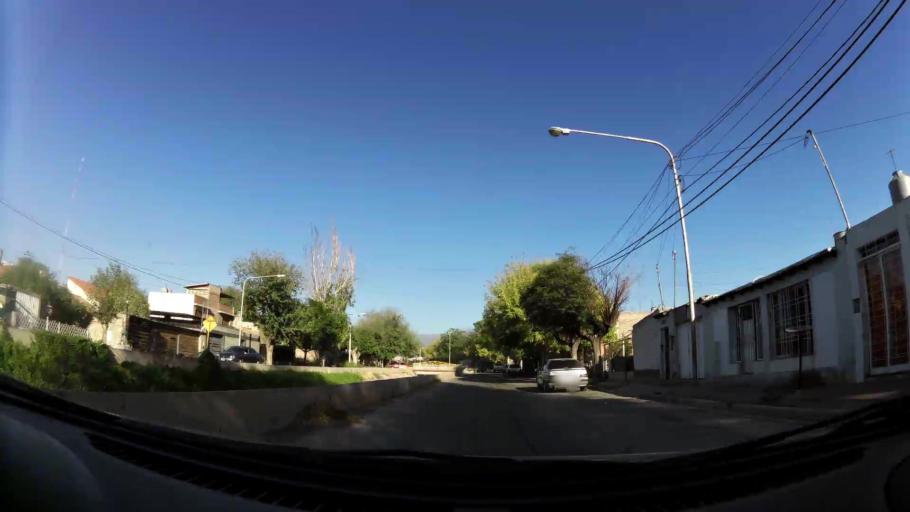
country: AR
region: Mendoza
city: Las Heras
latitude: -32.8618
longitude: -68.8300
